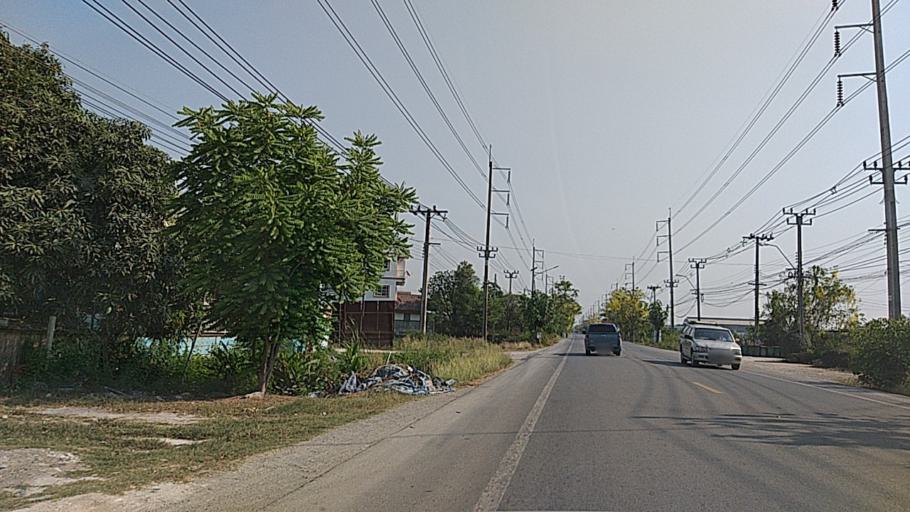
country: TH
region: Nonthaburi
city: Sai Noi
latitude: 14.0430
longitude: 100.3121
